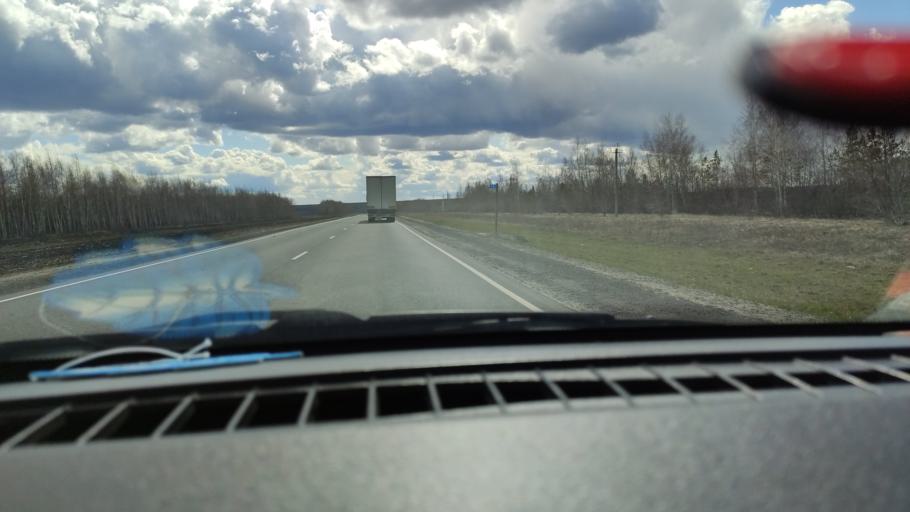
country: RU
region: Samara
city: Syzran'
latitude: 52.9860
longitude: 48.3173
